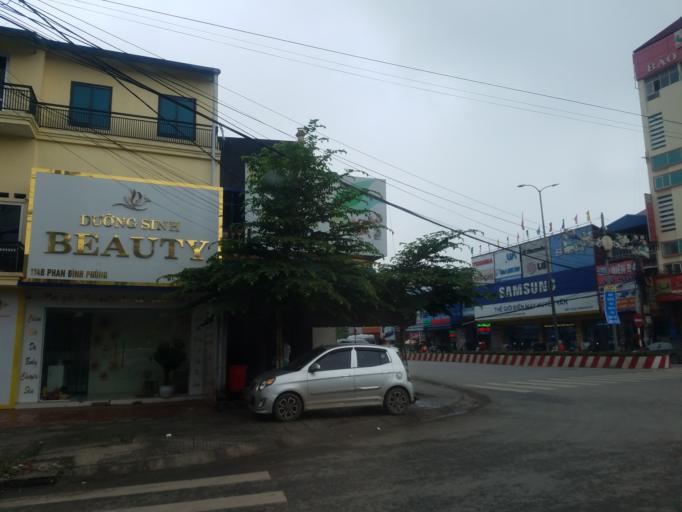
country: VN
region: Thai Nguyen
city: Thanh Pho Thai Nguyen
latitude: 21.5906
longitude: 105.8454
